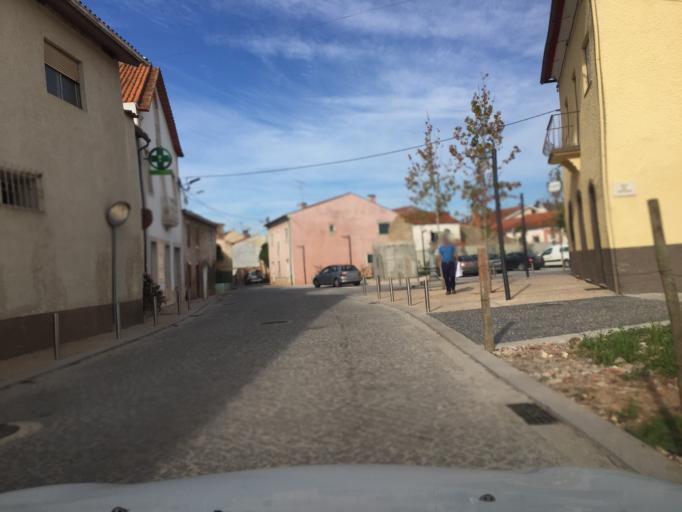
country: PT
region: Aveiro
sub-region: Anadia
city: Anadia
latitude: 40.4096
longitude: -8.3993
